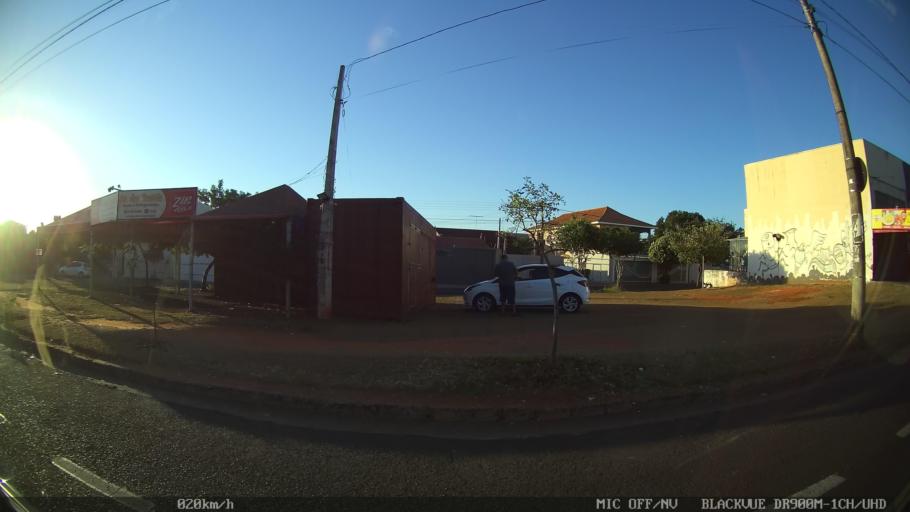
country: BR
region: Sao Paulo
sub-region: Sao Jose Do Rio Preto
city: Sao Jose do Rio Preto
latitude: -20.7796
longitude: -49.3698
